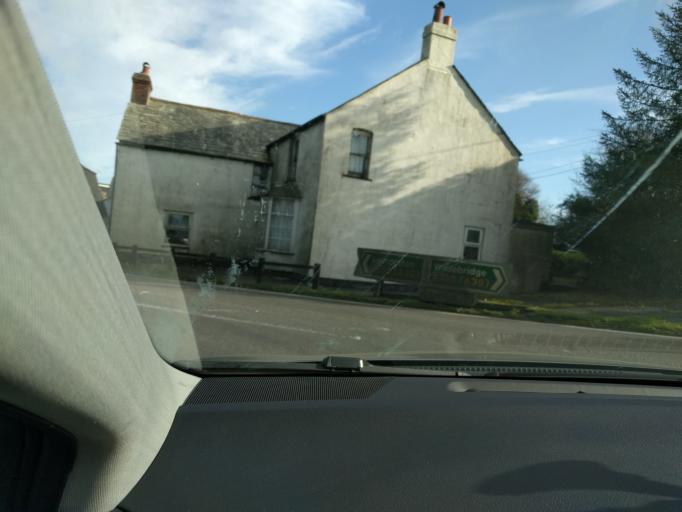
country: GB
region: England
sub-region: Cornwall
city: Jacobstow
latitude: 50.6616
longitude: -4.5767
